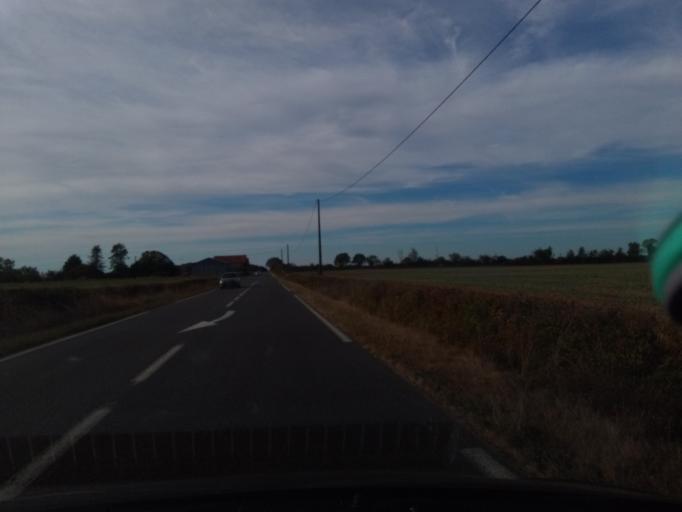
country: FR
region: Poitou-Charentes
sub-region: Departement de la Vienne
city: Saulge
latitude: 46.4069
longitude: 0.8902
